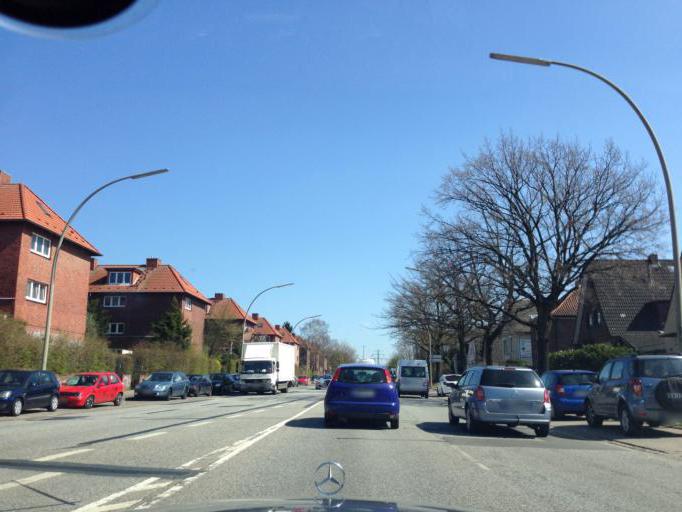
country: DE
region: Hamburg
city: Steilshoop
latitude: 53.6083
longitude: 10.0682
